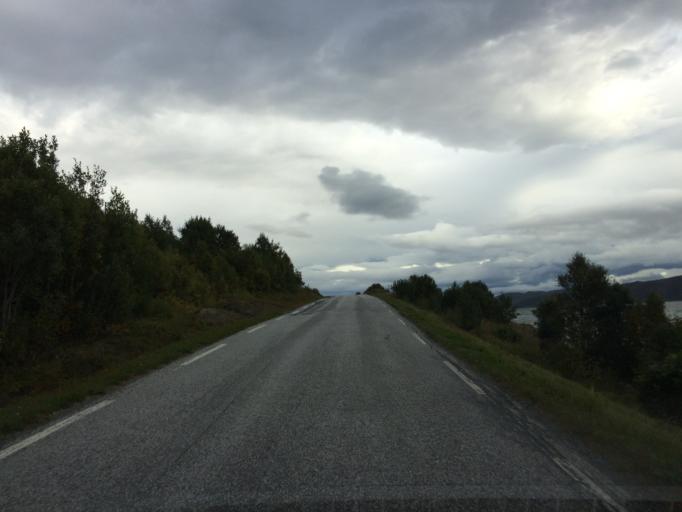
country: NO
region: Troms
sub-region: Lenvik
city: Finnsnes
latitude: 69.5230
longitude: 18.1790
